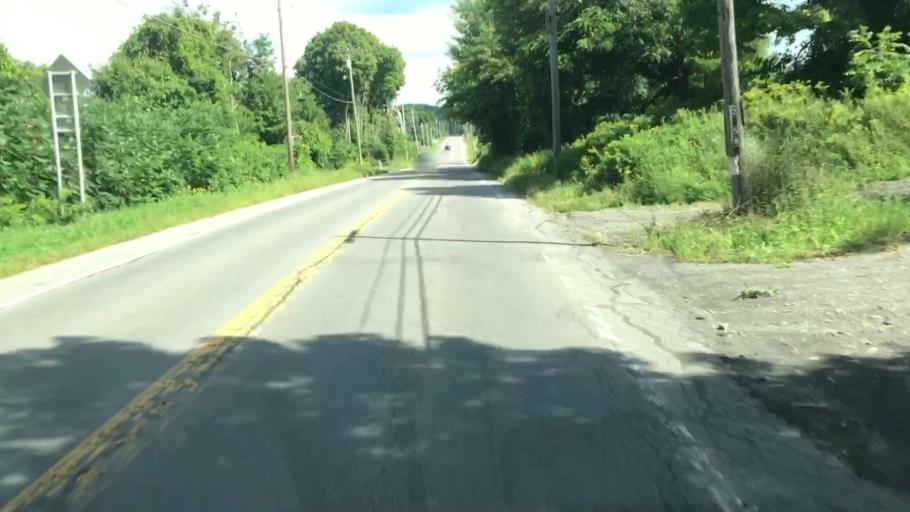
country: US
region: New York
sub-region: Onondaga County
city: Marcellus
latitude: 42.9839
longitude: -76.3056
